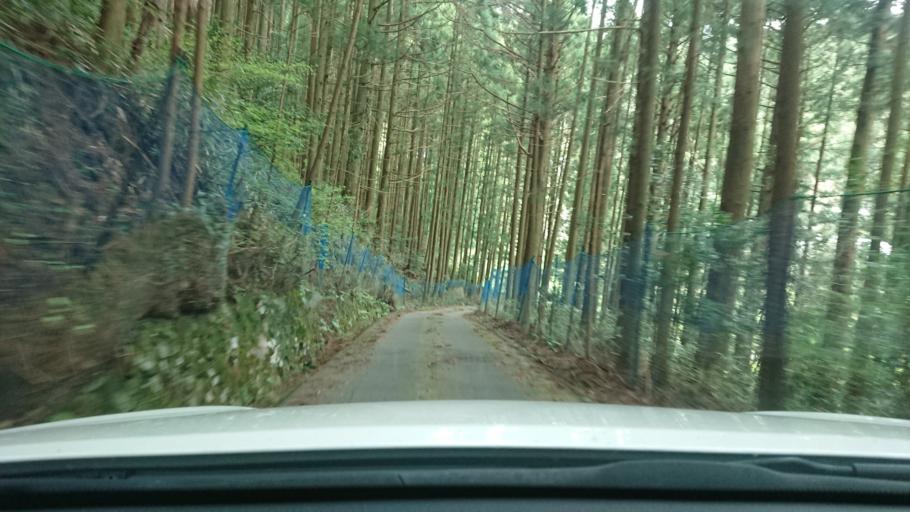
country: JP
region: Tokushima
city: Kamojimacho-jogejima
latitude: 33.8863
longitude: 134.3862
